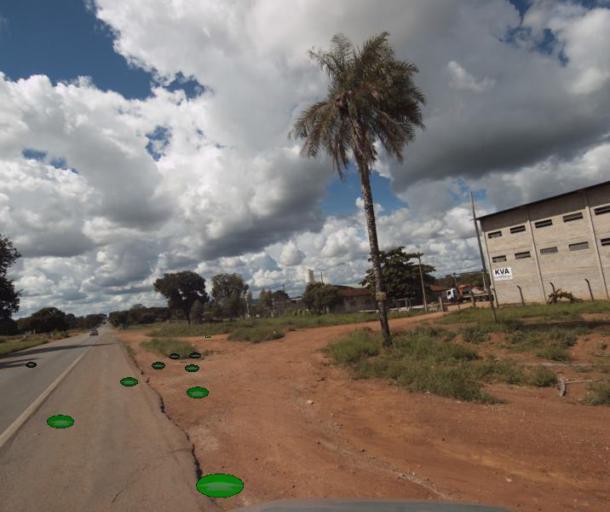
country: BR
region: Goias
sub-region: Porangatu
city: Porangatu
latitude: -13.4435
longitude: -49.1333
